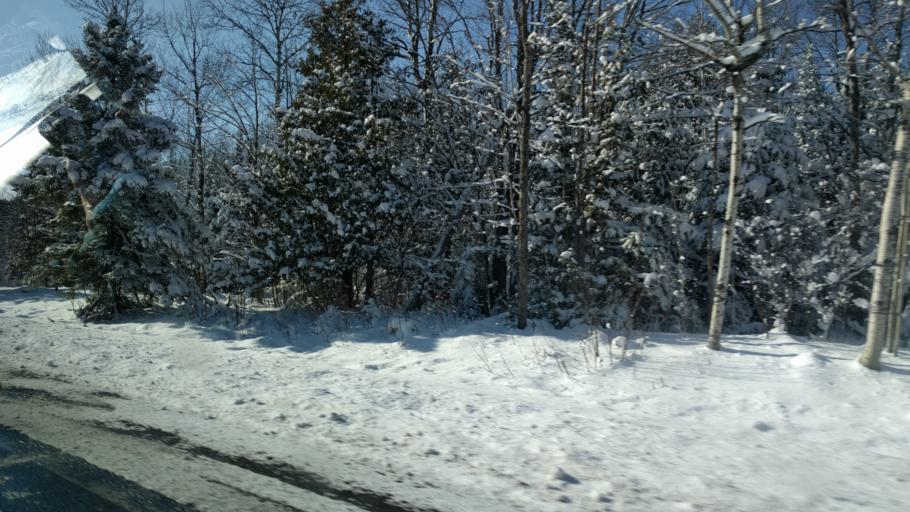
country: US
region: Wisconsin
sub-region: Iron County
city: Hurley
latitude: 46.3979
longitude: -90.3387
